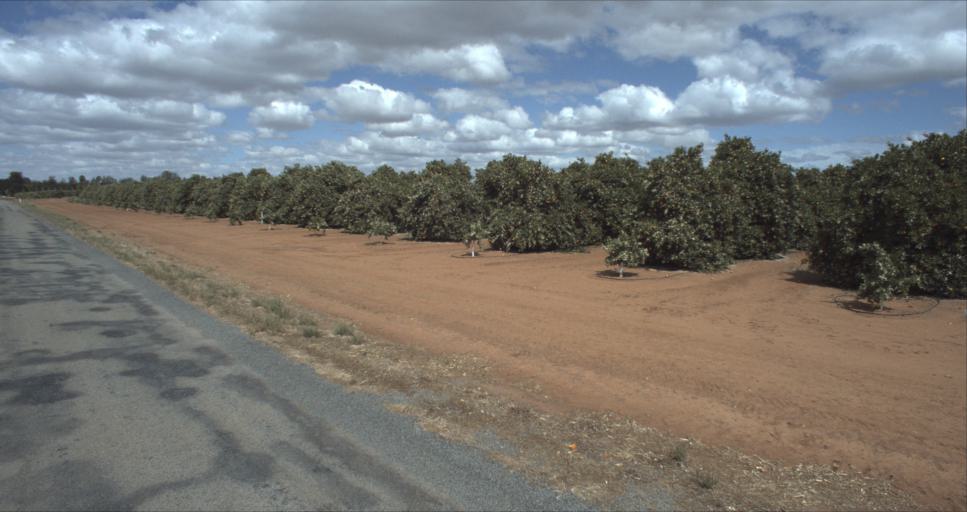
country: AU
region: New South Wales
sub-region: Leeton
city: Leeton
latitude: -34.5805
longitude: 146.4045
